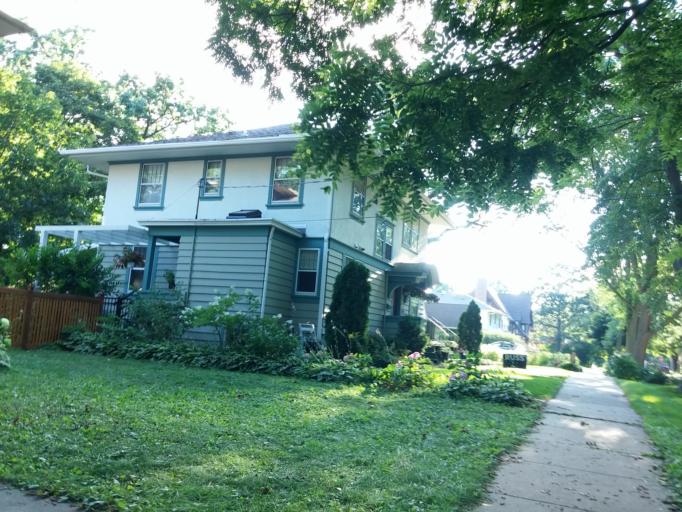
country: US
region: Wisconsin
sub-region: Dane County
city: Madison
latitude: 43.0687
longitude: -89.4194
